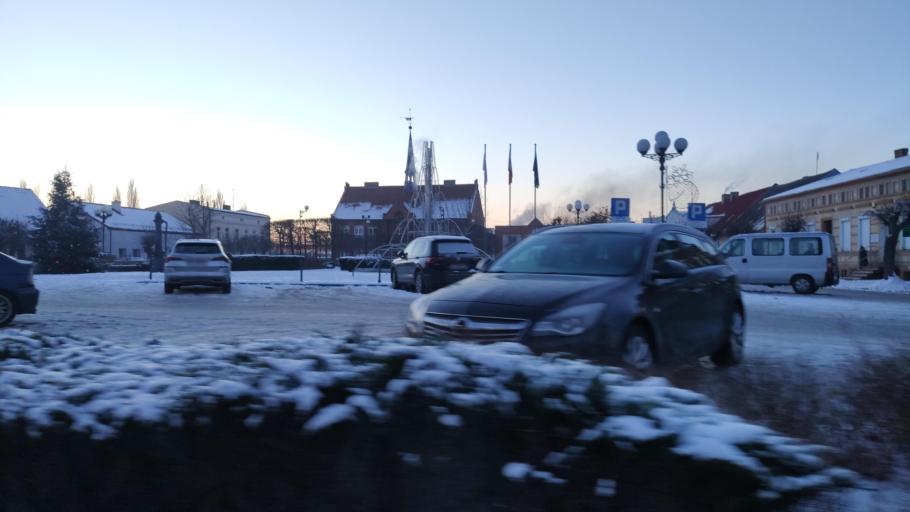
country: PL
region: Kujawsko-Pomorskie
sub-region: Powiat zninski
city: Barcin
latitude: 52.8642
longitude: 17.9458
